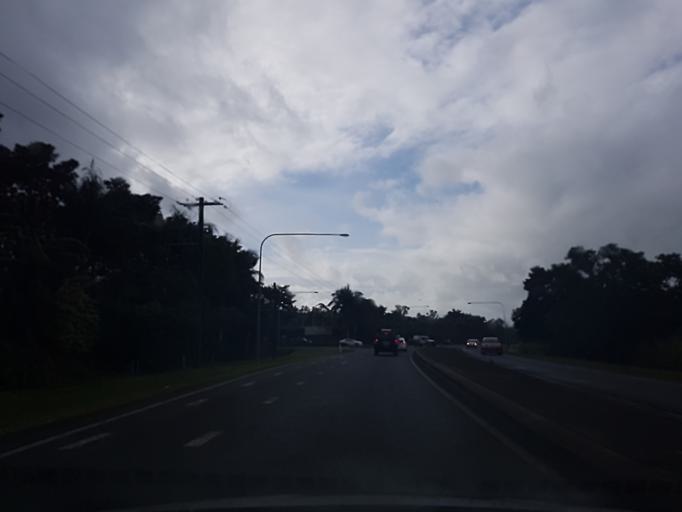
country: AU
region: Queensland
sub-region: Cairns
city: Trinity Beach
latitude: -16.7835
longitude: 145.6733
